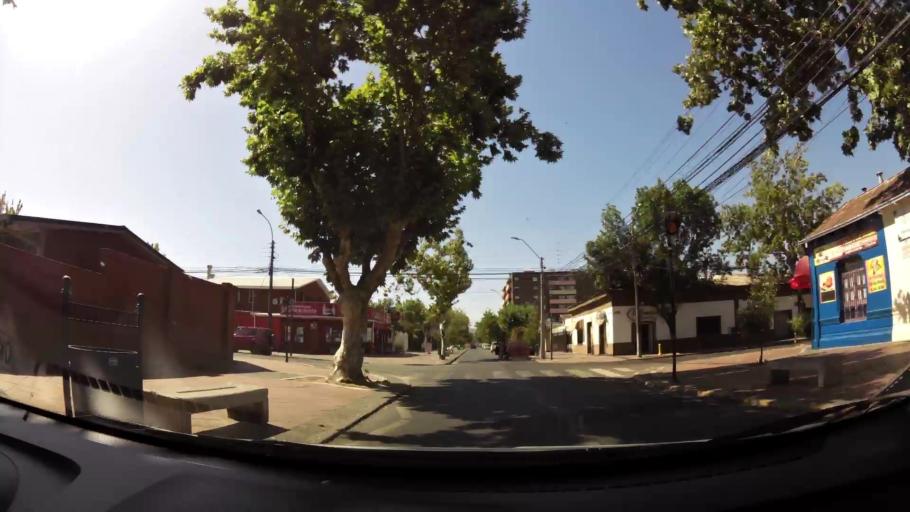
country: CL
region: Maule
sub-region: Provincia de Talca
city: Talca
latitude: -35.4198
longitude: -71.6579
